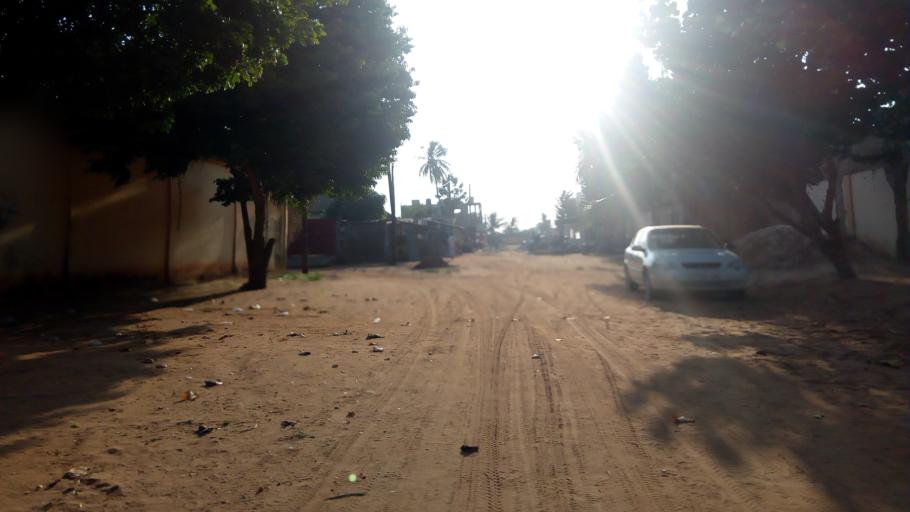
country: TG
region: Maritime
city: Lome
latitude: 6.1787
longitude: 1.1916
